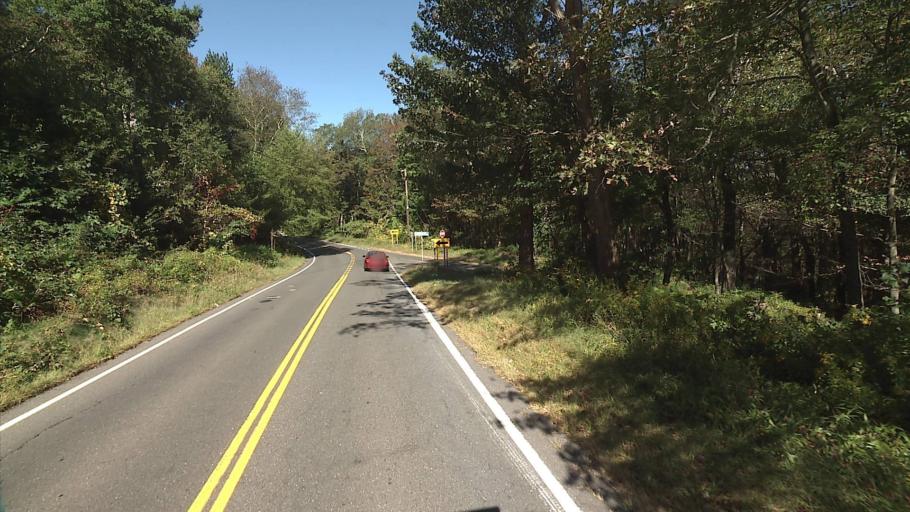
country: US
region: Connecticut
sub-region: Hartford County
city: Bristol
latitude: 41.7347
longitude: -72.9564
